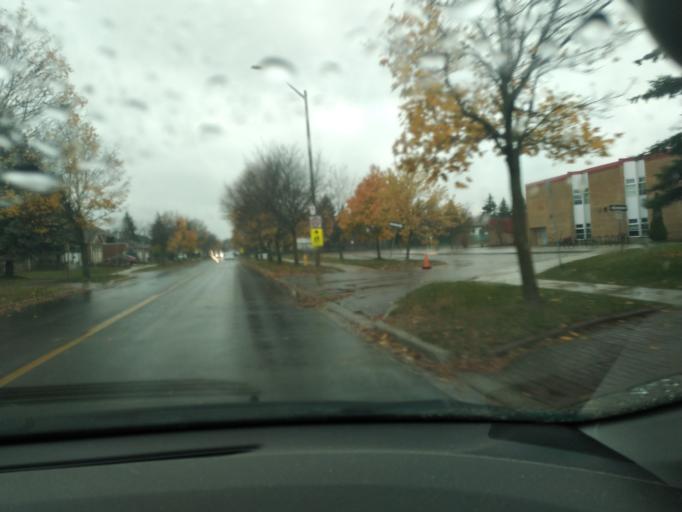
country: CA
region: Ontario
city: Markham
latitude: 43.8324
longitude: -79.2816
